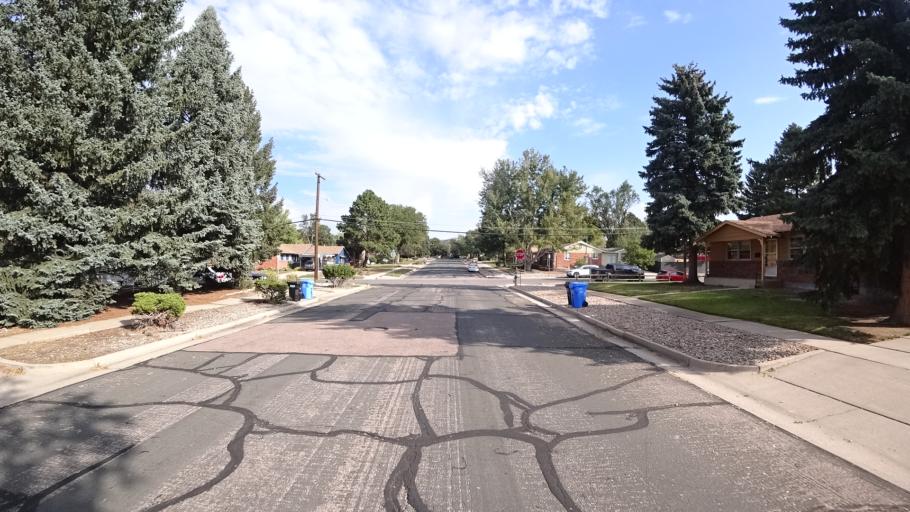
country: US
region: Colorado
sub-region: El Paso County
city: Colorado Springs
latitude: 38.8565
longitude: -104.7770
